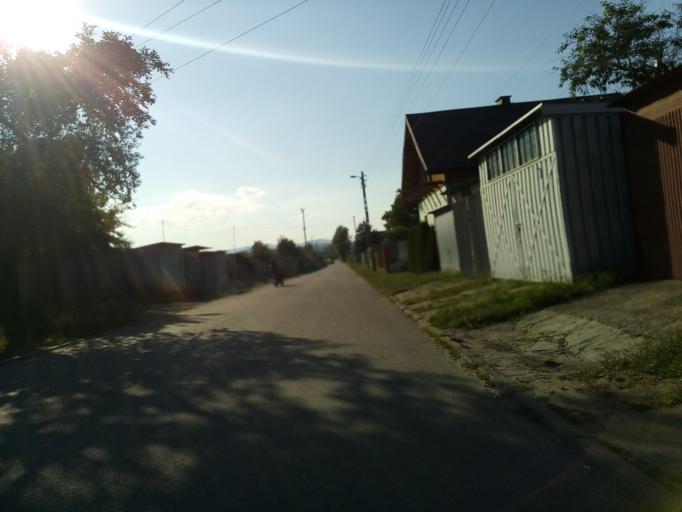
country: PL
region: Lesser Poland Voivodeship
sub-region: Powiat nowosadecki
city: Stary Sacz
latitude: 49.5674
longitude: 20.6256
